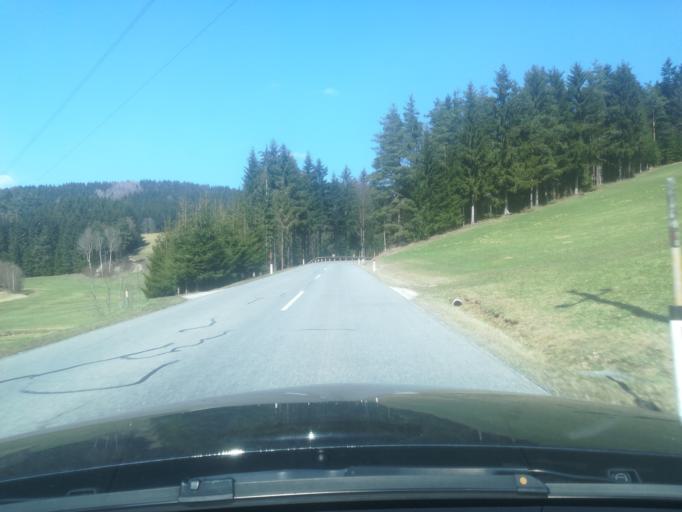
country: AT
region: Lower Austria
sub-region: Politischer Bezirk Zwettl
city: Langschlag
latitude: 48.4706
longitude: 14.7982
